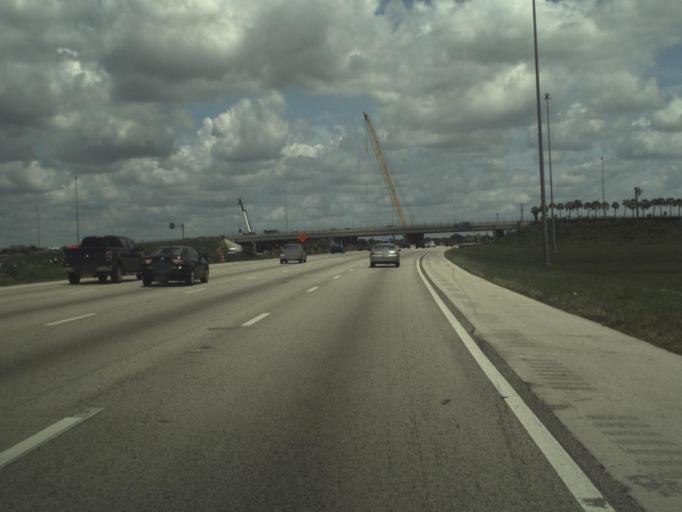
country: US
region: Florida
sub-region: Broward County
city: Sunshine Ranches
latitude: 26.0262
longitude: -80.3501
